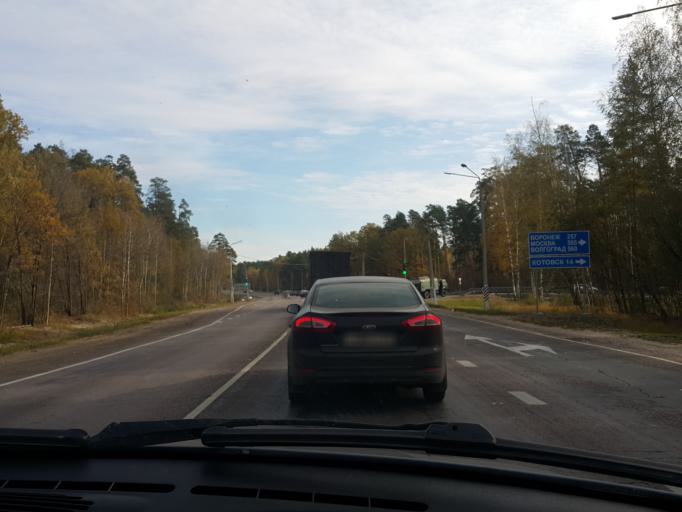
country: RU
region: Tambov
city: Donskoye
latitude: 52.7067
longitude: 41.5434
